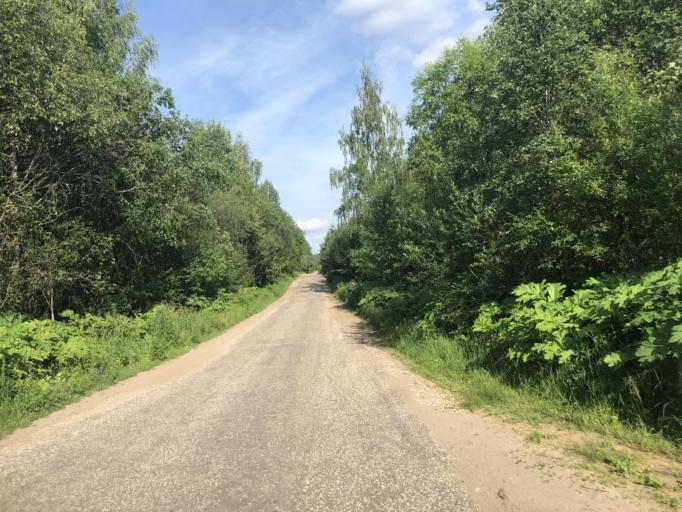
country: RU
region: Komi Republic
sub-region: Syktyvdinskiy Rayon
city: Syktyvkar
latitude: 61.6470
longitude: 50.7591
